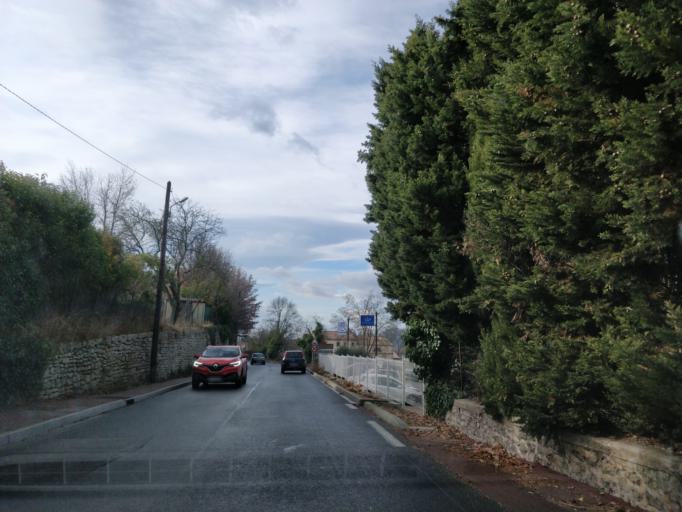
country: FR
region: Languedoc-Roussillon
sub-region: Departement du Gard
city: Villevieille
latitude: 43.7938
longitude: 4.0931
